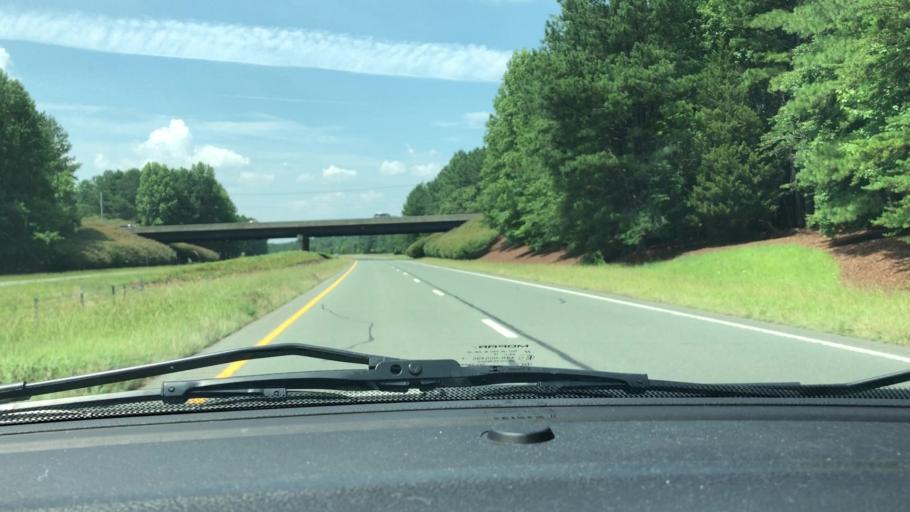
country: US
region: North Carolina
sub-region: Chatham County
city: Siler City
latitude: 35.7327
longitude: -79.4313
